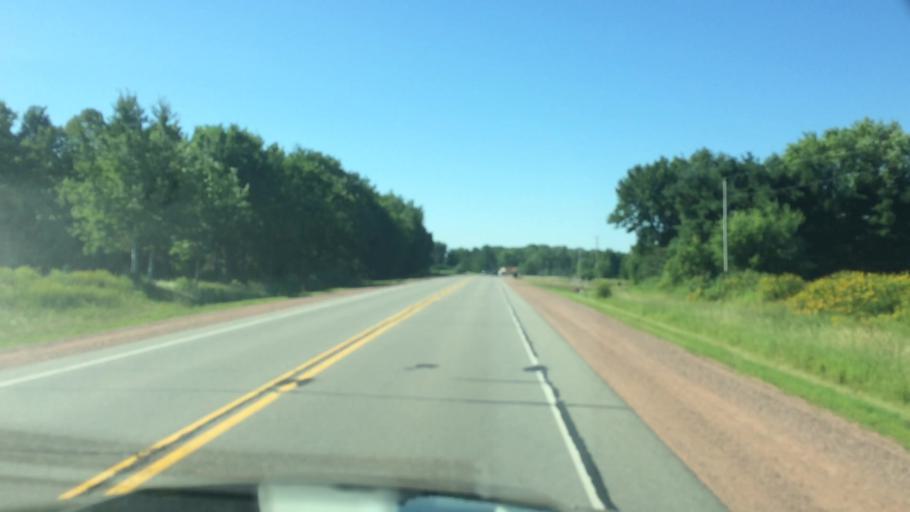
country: US
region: Wisconsin
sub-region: Marathon County
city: Stratford
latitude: 44.7401
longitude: -90.0794
